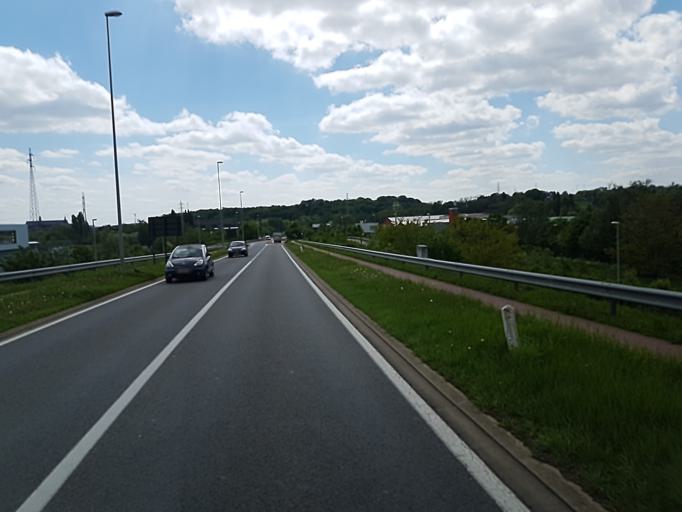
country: BE
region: Flanders
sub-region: Provincie Vlaams-Brabant
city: Diest
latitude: 50.9936
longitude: 5.0404
